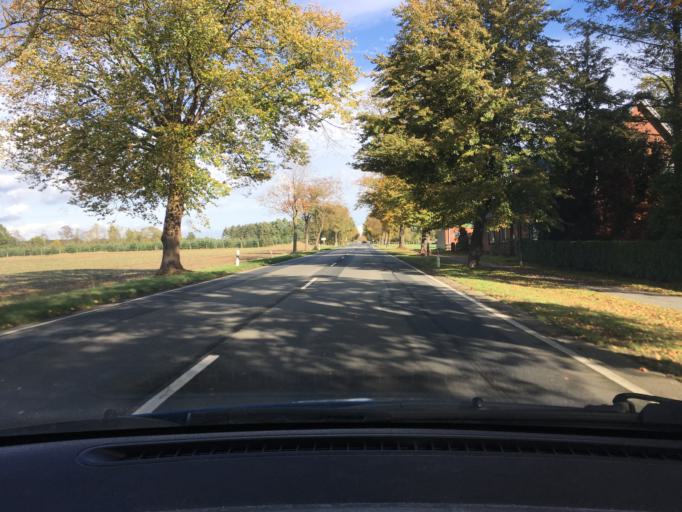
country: DE
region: Lower Saxony
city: Wistedt
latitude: 53.2740
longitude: 9.6873
